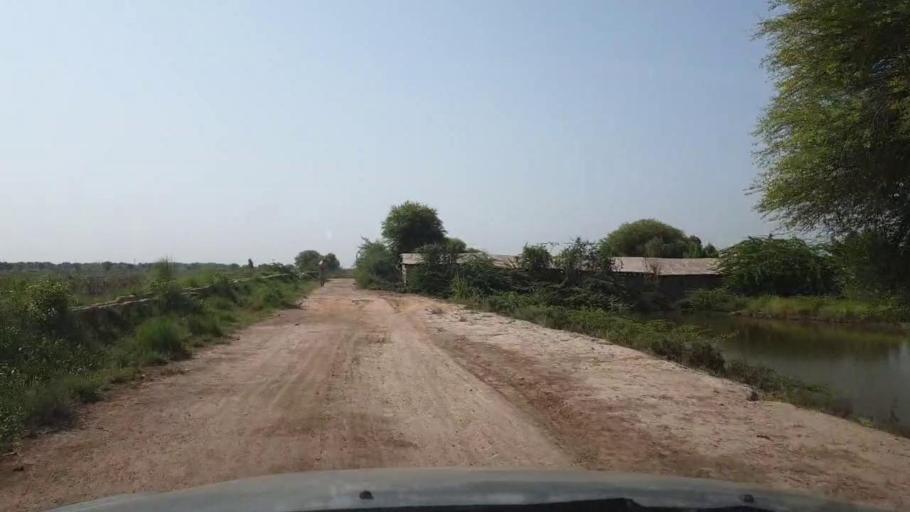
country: PK
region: Sindh
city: Tando Ghulam Ali
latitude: 25.1354
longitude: 68.8729
